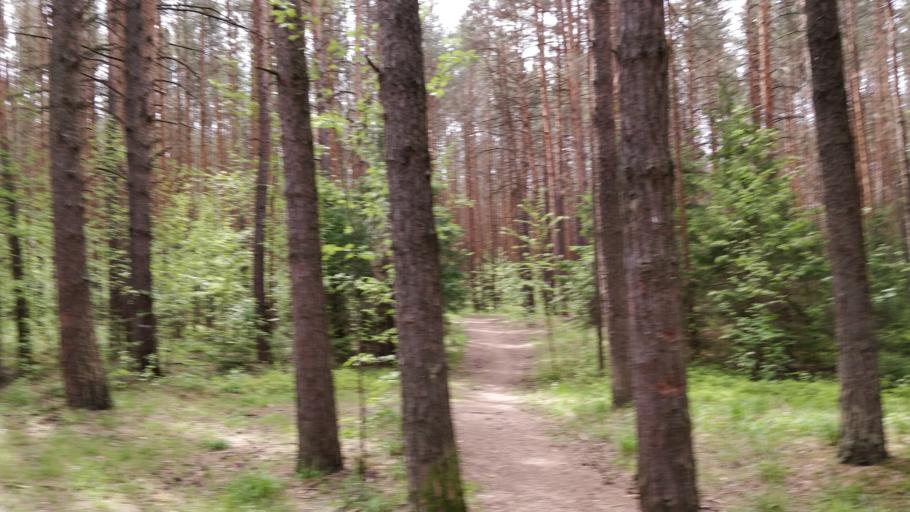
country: RU
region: Perm
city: Kondratovo
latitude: 57.9831
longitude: 56.1437
